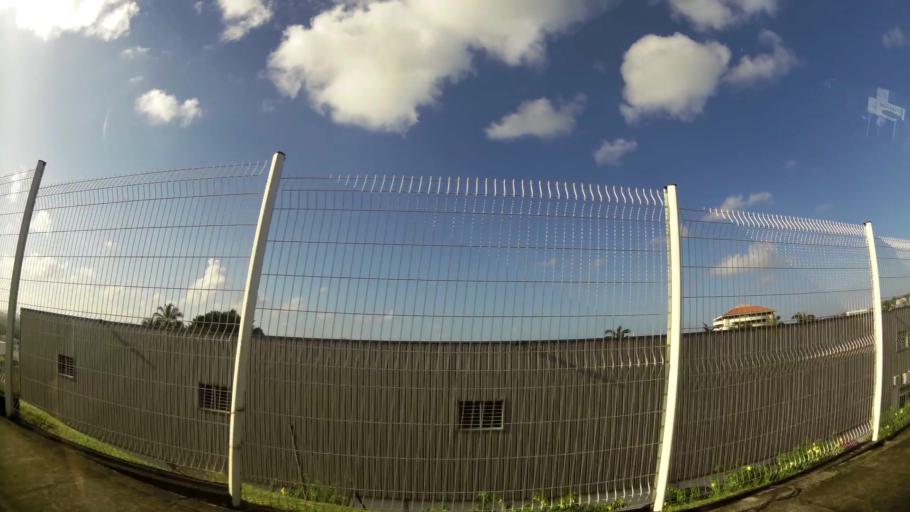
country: MQ
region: Martinique
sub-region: Martinique
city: Le Lamentin
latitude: 14.6207
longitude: -61.0188
